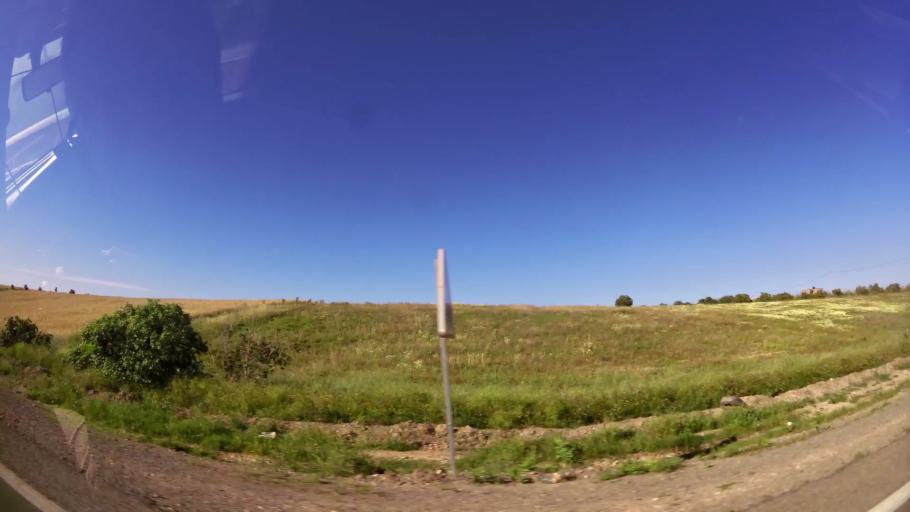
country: MA
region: Oriental
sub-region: Berkane-Taourirt
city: Ahfir
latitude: 34.9793
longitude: -2.1362
